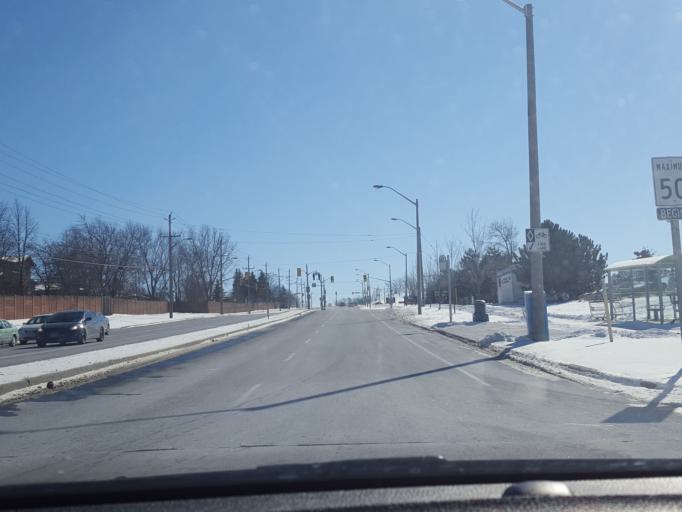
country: CA
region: Ontario
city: Kitchener
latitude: 43.4316
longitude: -80.5256
